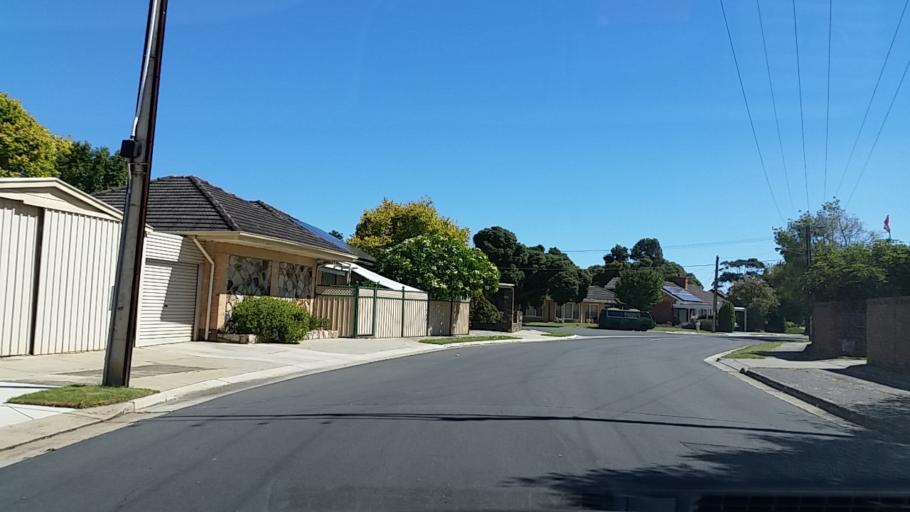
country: AU
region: South Australia
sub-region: Charles Sturt
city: Henley Beach
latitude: -34.9228
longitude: 138.5115
